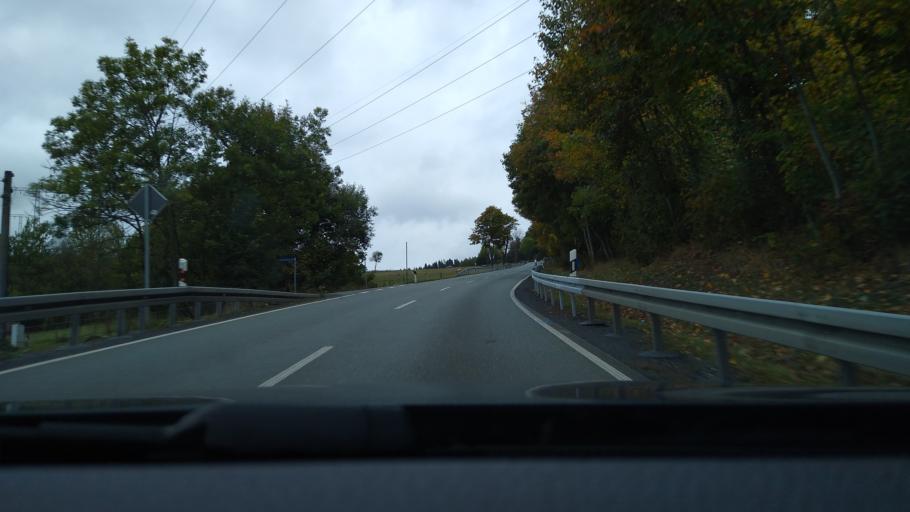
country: DE
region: Thuringia
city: Neuhaus am Rennweg
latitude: 50.5223
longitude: 11.1548
